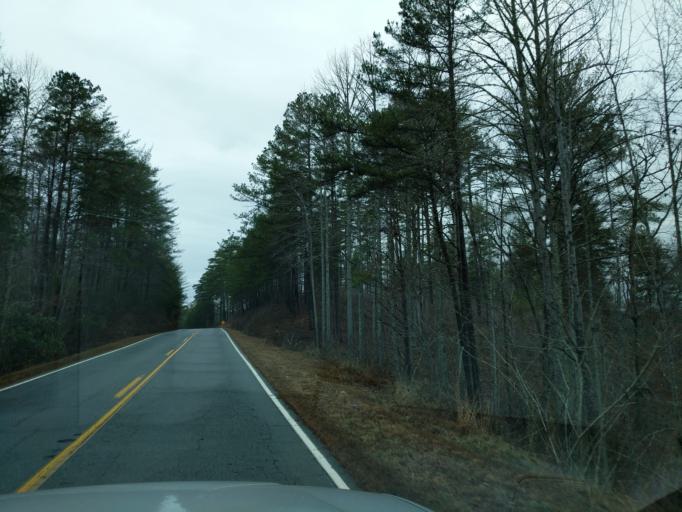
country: US
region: South Carolina
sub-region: Oconee County
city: Walhalla
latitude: 34.7889
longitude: -83.1995
